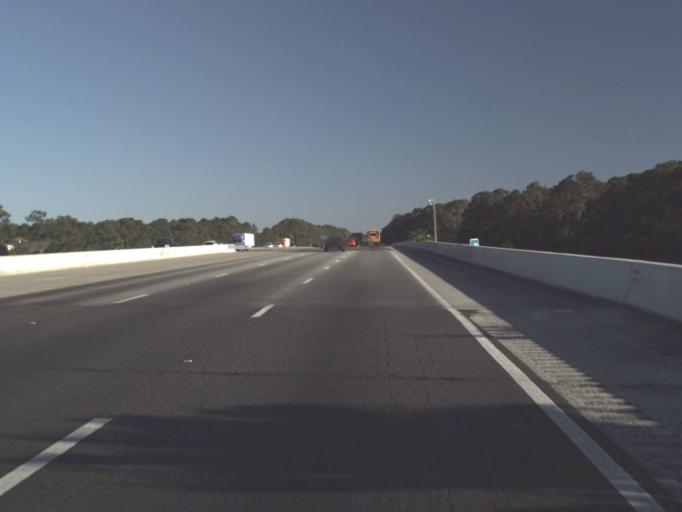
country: US
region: Florida
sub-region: Flagler County
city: Flagler Beach
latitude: 29.4763
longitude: -81.1841
